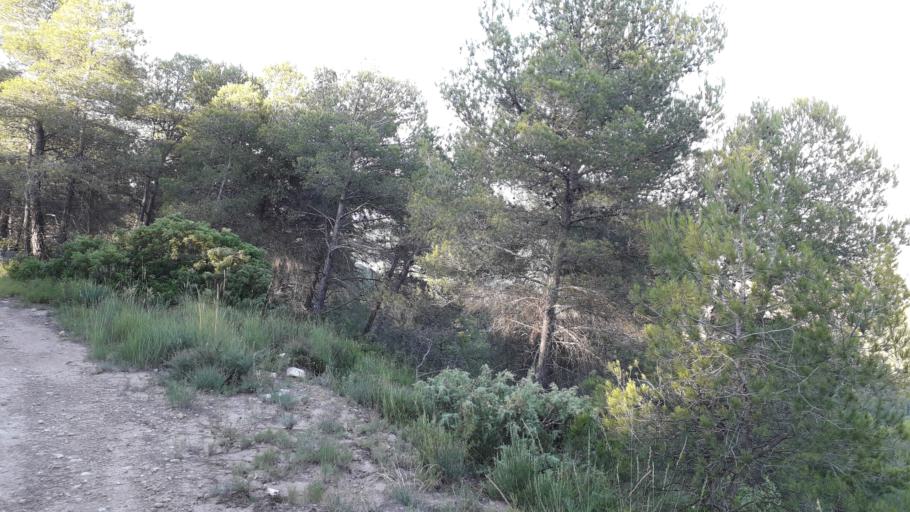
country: ES
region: Catalonia
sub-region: Provincia de Barcelona
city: Sant Marti de Tous
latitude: 41.5763
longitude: 1.4902
